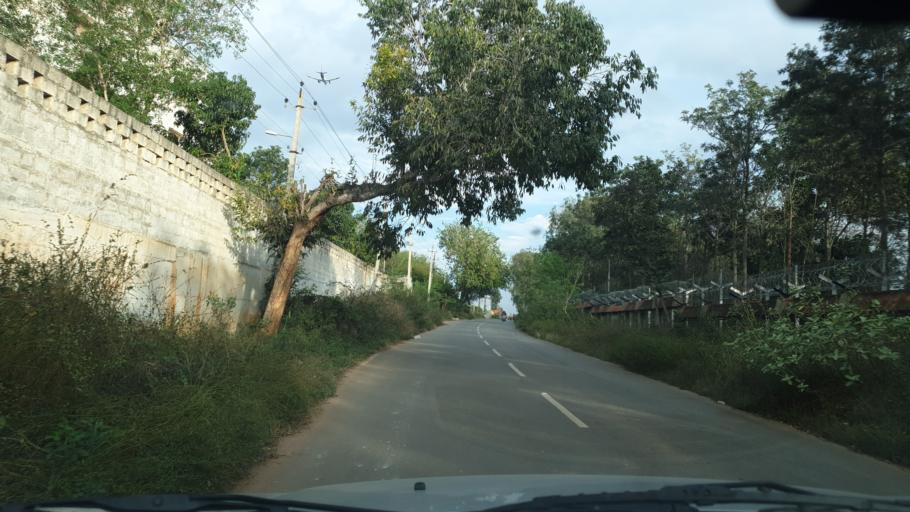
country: IN
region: Karnataka
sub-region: Bangalore Rural
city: Devanhalli
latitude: 13.1892
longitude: 77.6399
